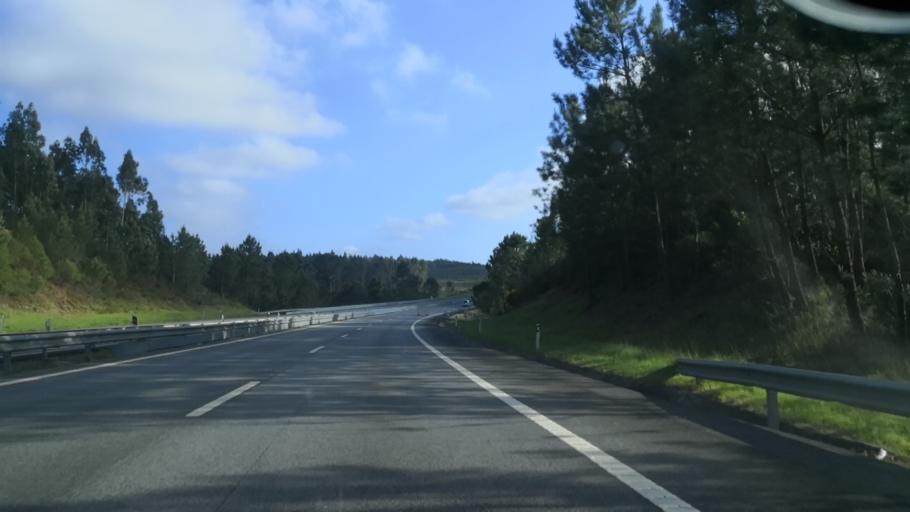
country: PT
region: Leiria
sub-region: Bombarral
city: Bombarral
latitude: 39.2084
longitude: -9.1883
